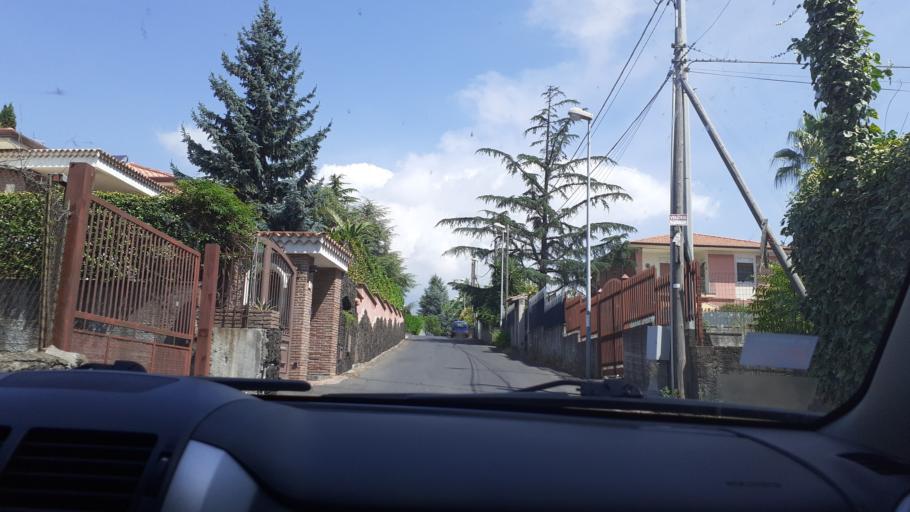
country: IT
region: Sicily
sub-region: Catania
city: Nicolosi
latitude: 37.6178
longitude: 15.0314
